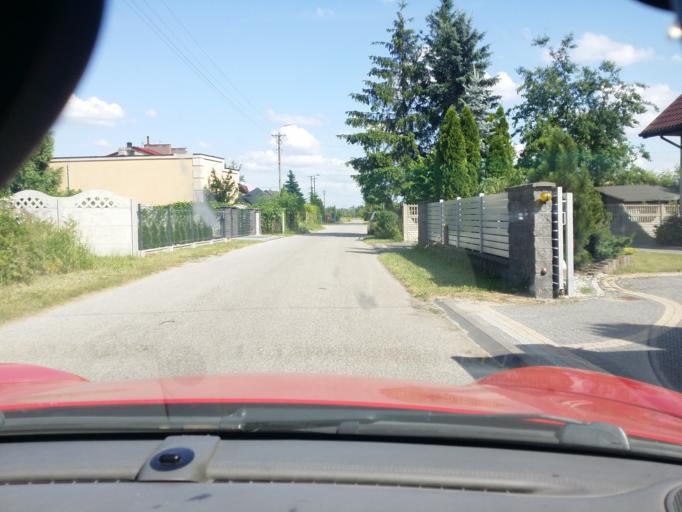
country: PL
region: Masovian Voivodeship
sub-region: Powiat radomski
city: Trablice
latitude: 51.3471
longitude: 21.1403
